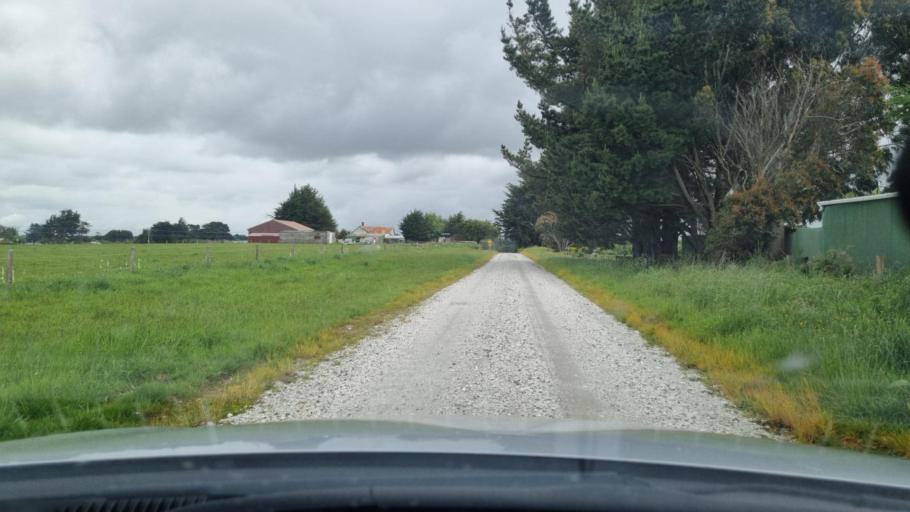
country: NZ
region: Southland
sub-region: Invercargill City
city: Invercargill
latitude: -46.4486
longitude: 168.3938
